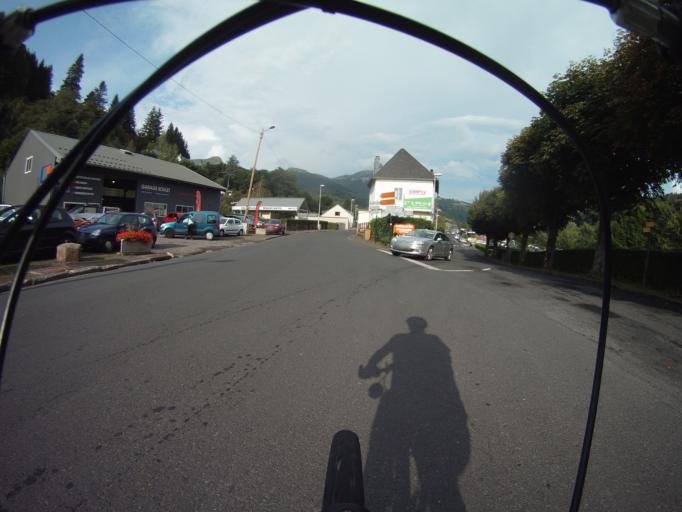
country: FR
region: Auvergne
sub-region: Departement du Puy-de-Dome
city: La Bourboule
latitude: 45.5906
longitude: 2.7482
